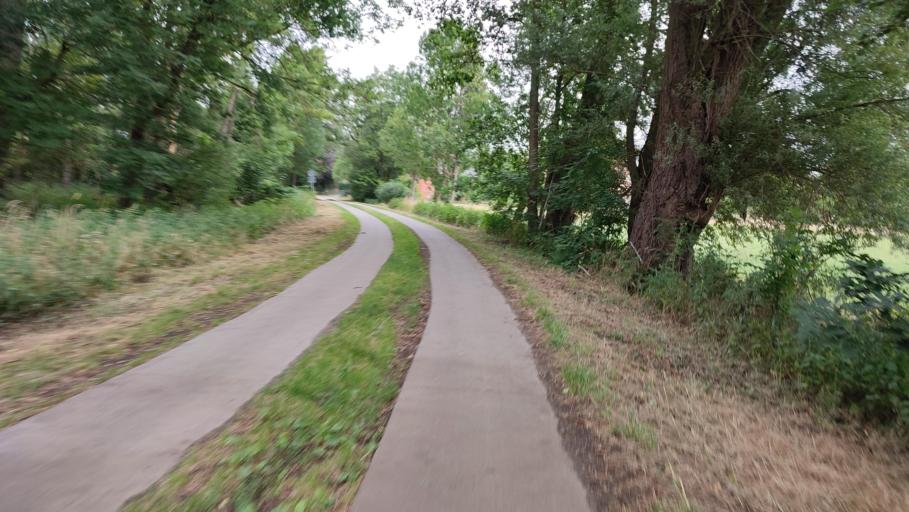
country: DE
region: Lower Saxony
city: Hitzacker
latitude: 53.1798
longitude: 11.1037
